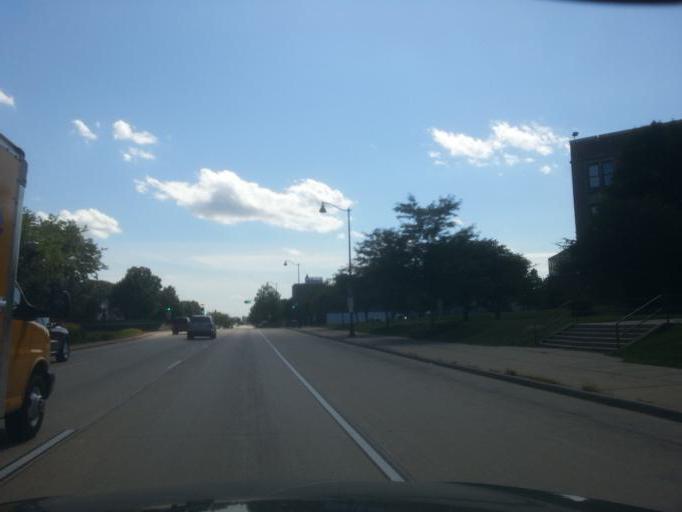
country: US
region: Wisconsin
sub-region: Dane County
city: Maple Bluff
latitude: 43.0970
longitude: -89.3532
